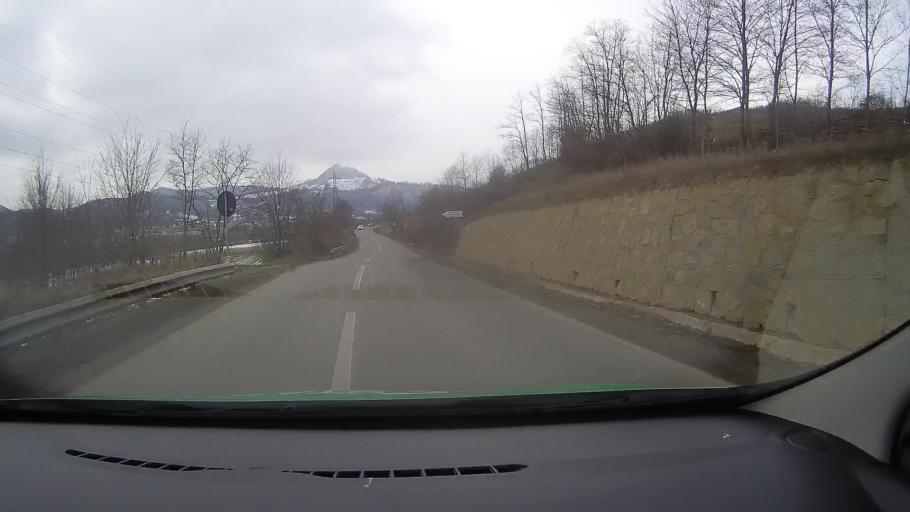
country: RO
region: Alba
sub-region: Oras Zlatna
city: Fenes
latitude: 46.0908
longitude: 23.2832
